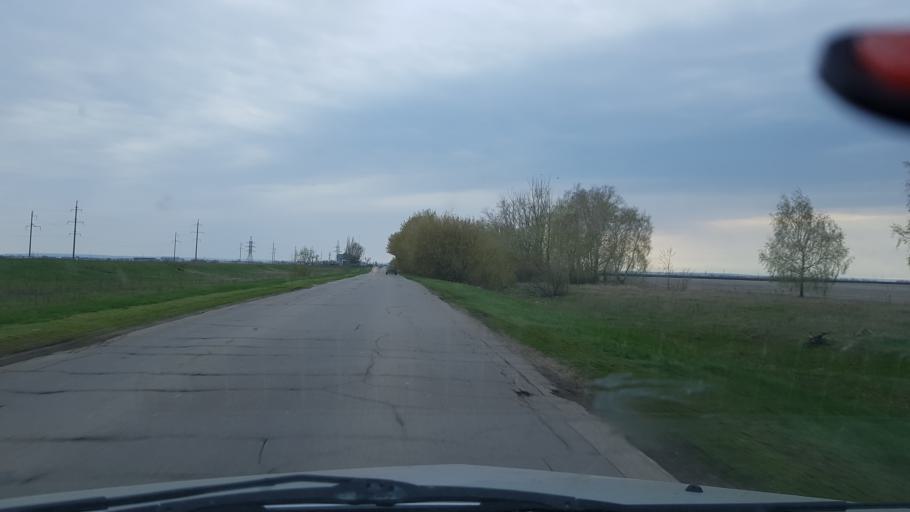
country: RU
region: Samara
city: Khryashchevka
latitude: 53.6701
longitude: 49.1158
